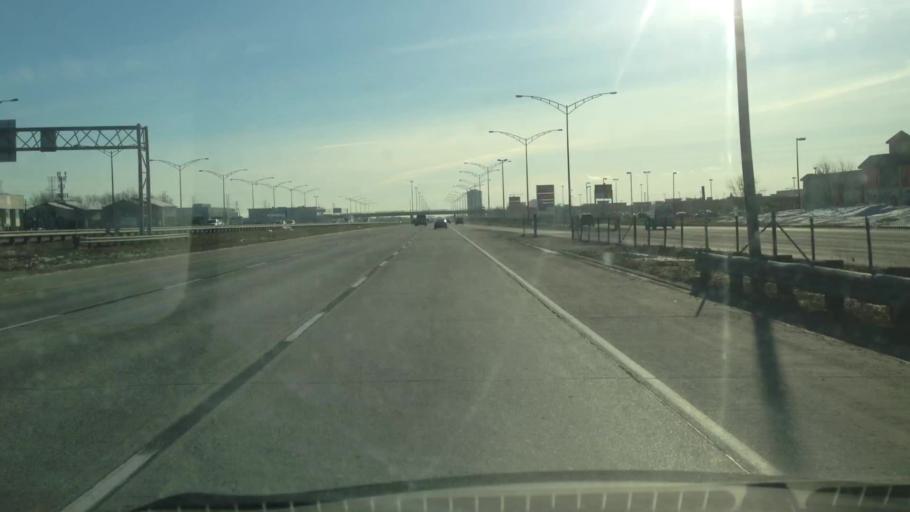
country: CA
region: Quebec
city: Dollard-Des Ormeaux
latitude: 45.5359
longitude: -73.7893
